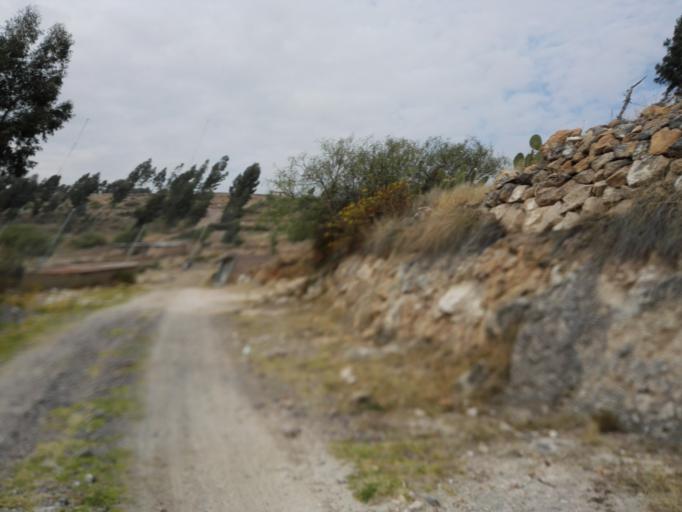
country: PE
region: Ayacucho
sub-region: Provincia de Huamanga
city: Ayacucho
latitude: -13.1482
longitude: -74.2374
